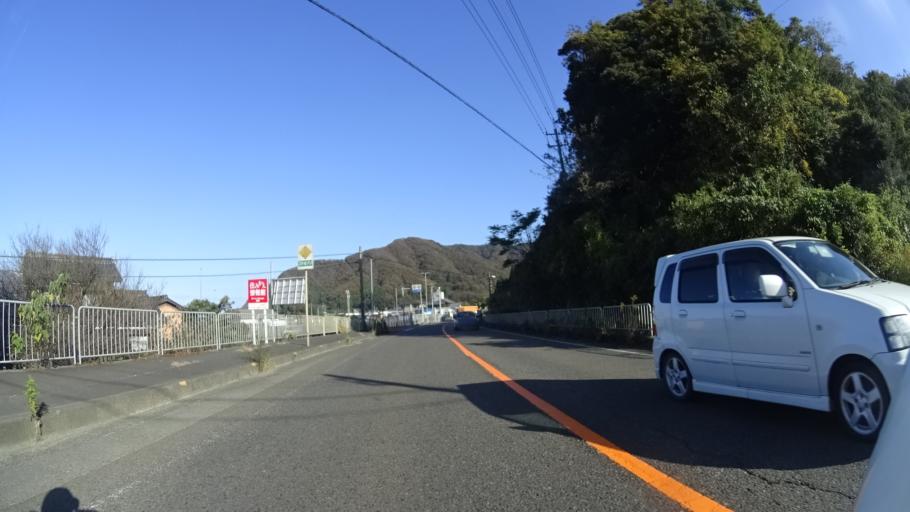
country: JP
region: Fukui
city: Tsuruga
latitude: 35.6808
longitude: 136.0854
